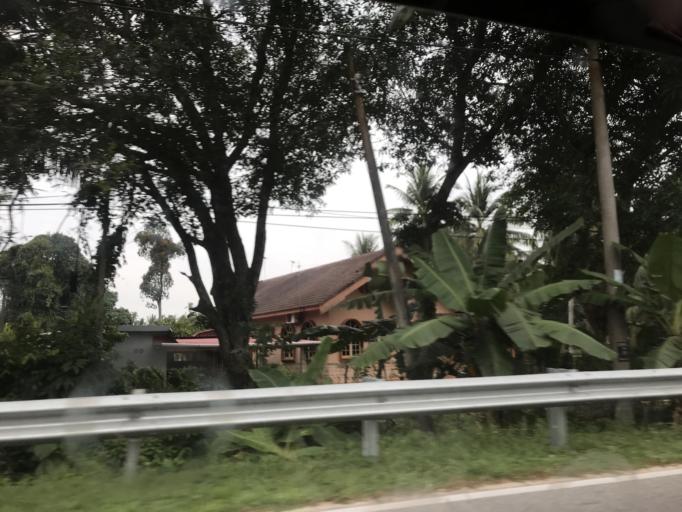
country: MY
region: Kelantan
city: Kota Bharu
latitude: 6.1658
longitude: 102.2270
